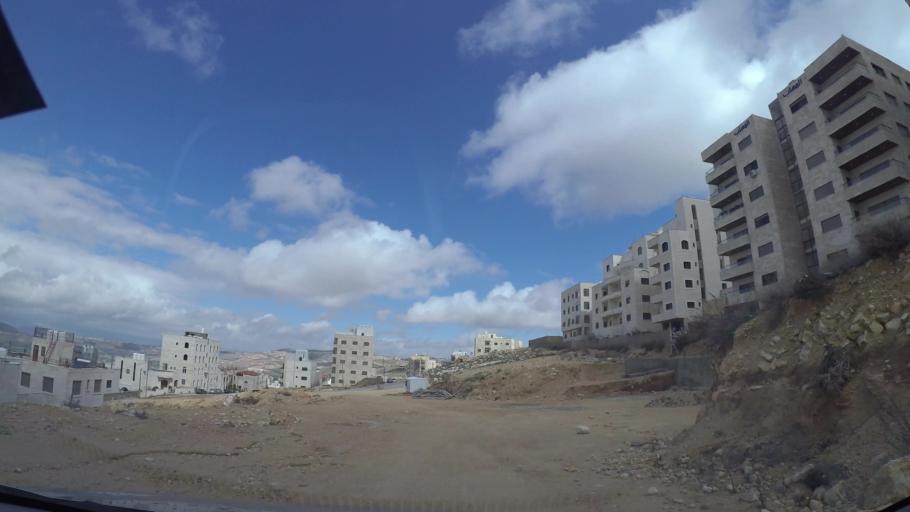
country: JO
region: Amman
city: Al Jubayhah
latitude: 32.0635
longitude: 35.8708
